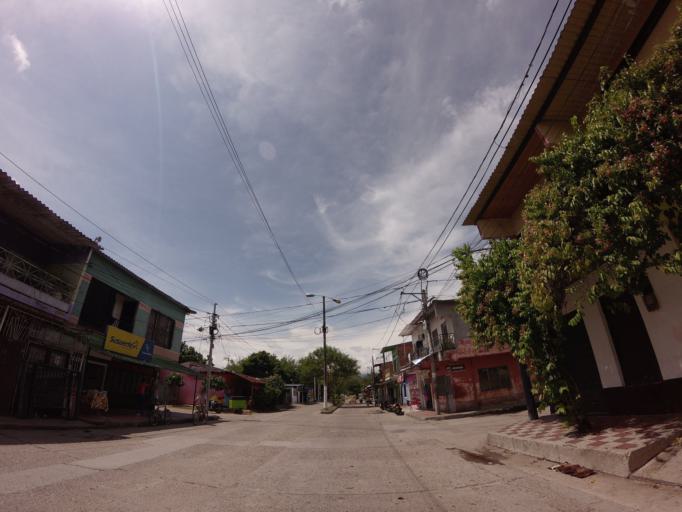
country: CO
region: Cundinamarca
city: Puerto Salgar
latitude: 5.4758
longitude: -74.6728
